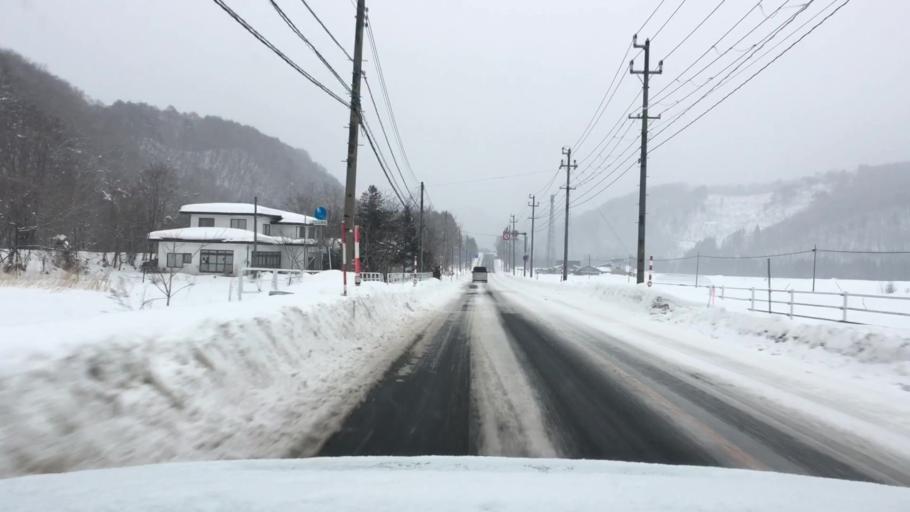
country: JP
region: Akita
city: Hanawa
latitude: 40.0581
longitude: 141.0111
